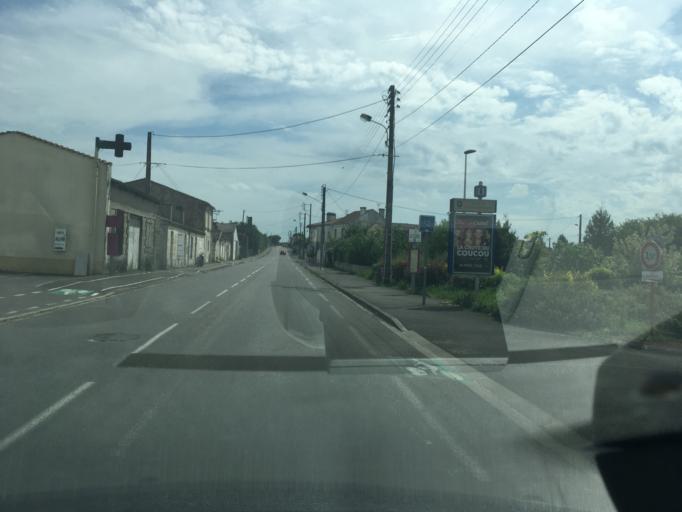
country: FR
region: Poitou-Charentes
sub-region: Departement de la Charente
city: Chateaubernard
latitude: 45.6806
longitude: -0.3285
